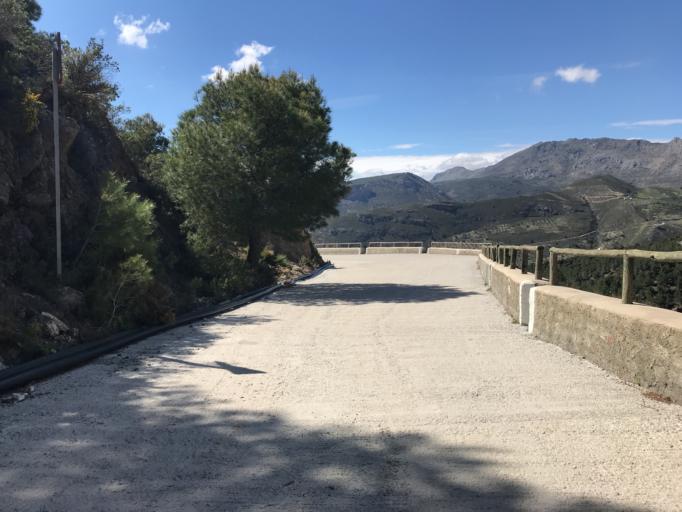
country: ES
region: Andalusia
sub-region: Provincia de Malaga
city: Alcaucin
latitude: 36.9175
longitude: -4.1000
